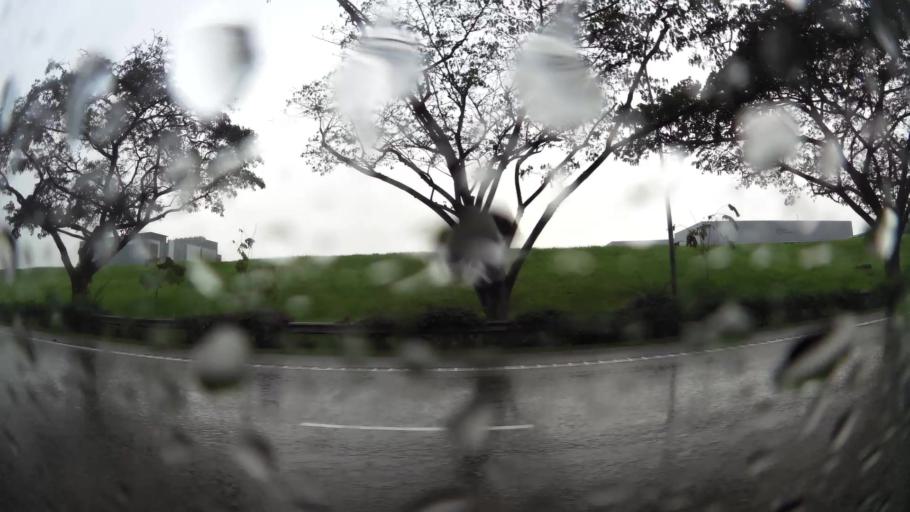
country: MY
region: Johor
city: Kampung Pasir Gudang Baru
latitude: 1.3782
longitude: 103.9241
